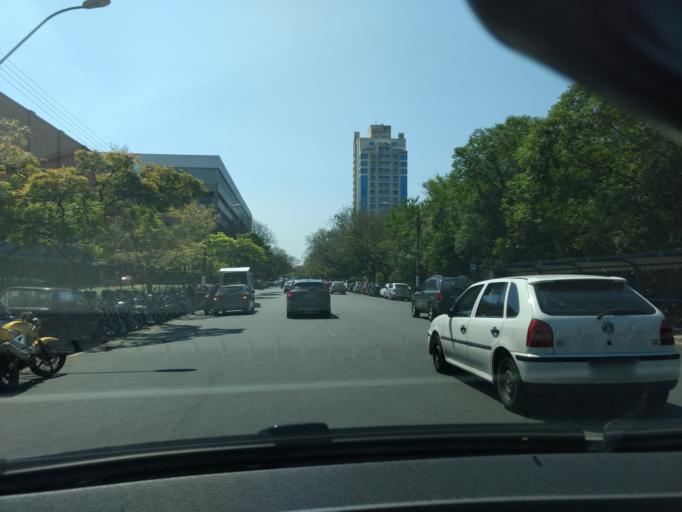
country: BR
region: Rio Grande do Sul
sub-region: Porto Alegre
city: Porto Alegre
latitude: -30.0253
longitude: -51.1613
